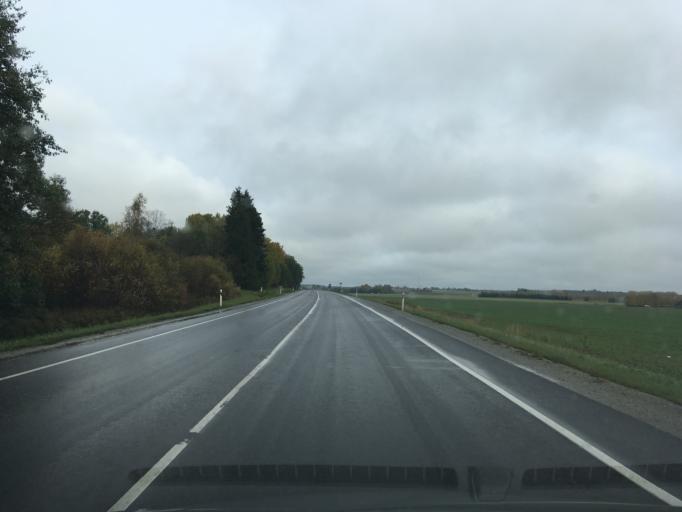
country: EE
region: Harju
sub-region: Saue linn
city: Saue
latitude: 59.3380
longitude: 24.4802
